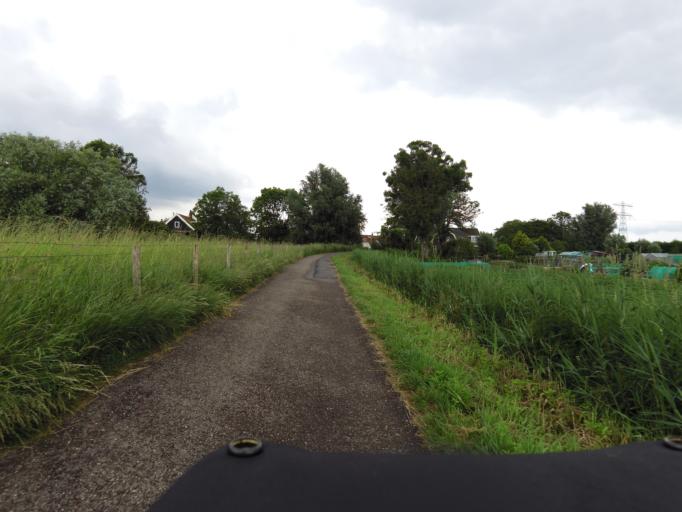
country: NL
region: South Holland
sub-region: Gemeente Albrandswaard
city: Rhoon
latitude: 51.8544
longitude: 4.3884
